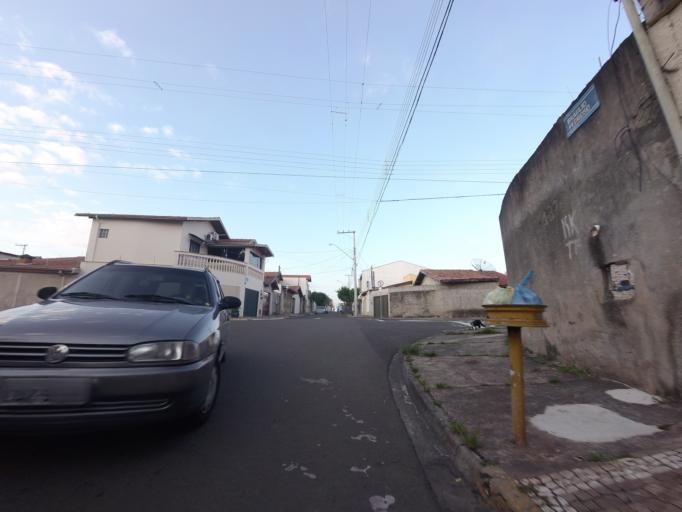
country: BR
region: Sao Paulo
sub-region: Piracicaba
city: Piracicaba
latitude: -22.7593
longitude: -47.6106
